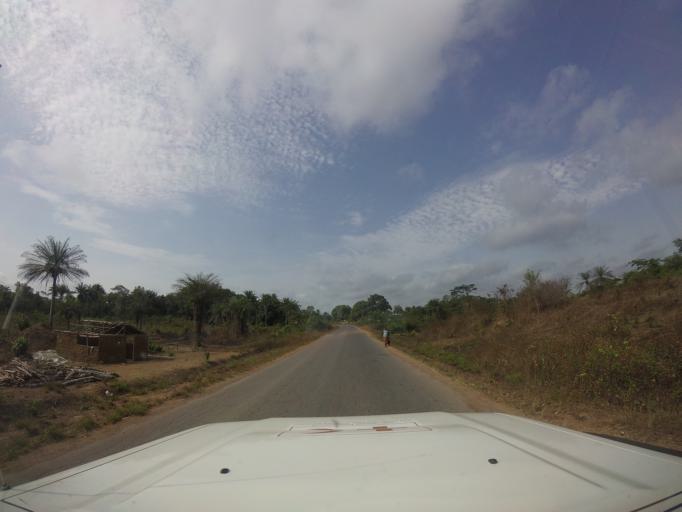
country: LR
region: Bomi
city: Tubmanburg
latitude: 6.7871
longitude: -10.8442
